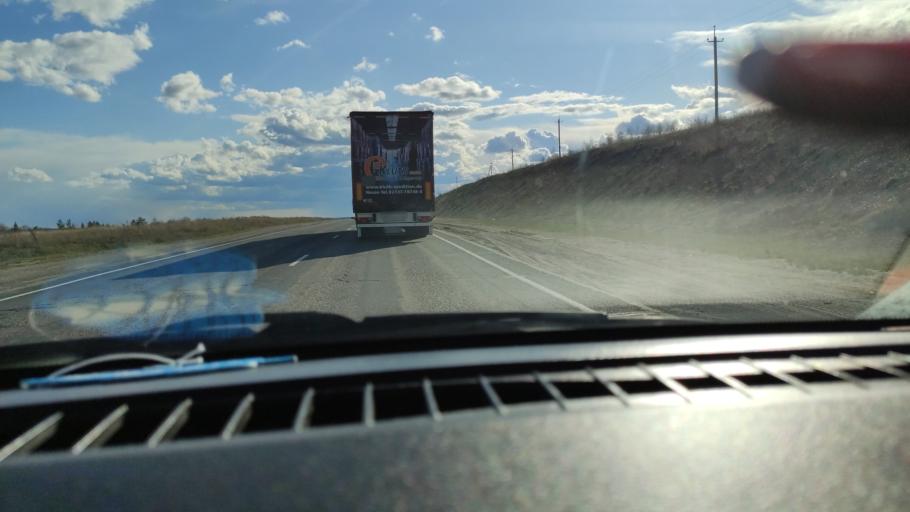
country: RU
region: Saratov
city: Sinodskoye
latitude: 52.0703
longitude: 46.7767
